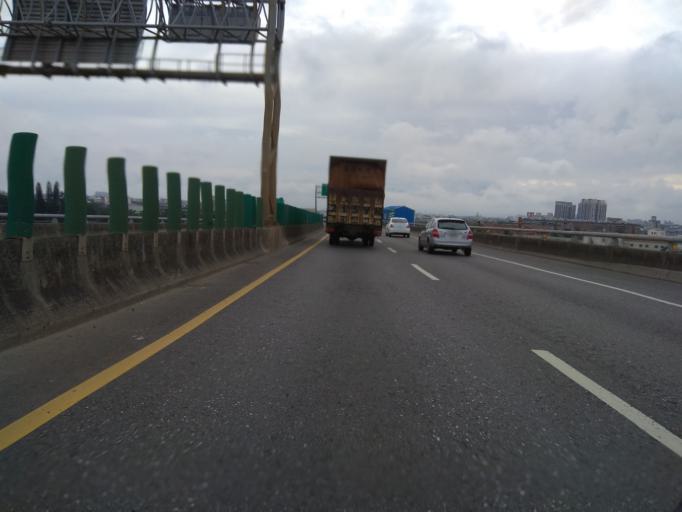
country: TW
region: Taiwan
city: Daxi
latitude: 24.9292
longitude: 121.2041
